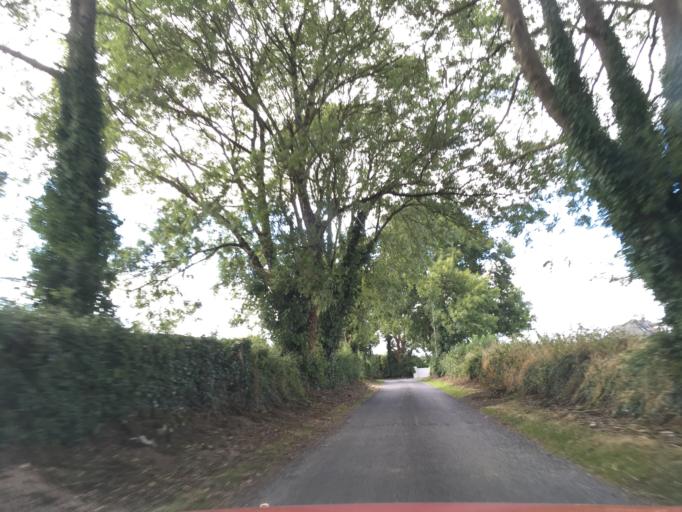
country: IE
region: Munster
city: Cashel
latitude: 52.4953
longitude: -7.9230
